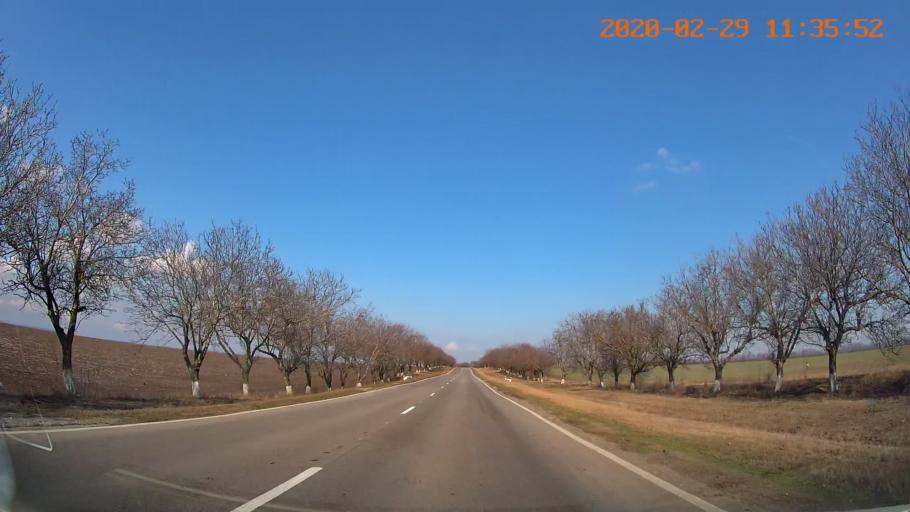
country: MD
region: Rezina
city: Saharna
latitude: 47.5872
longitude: 29.0604
